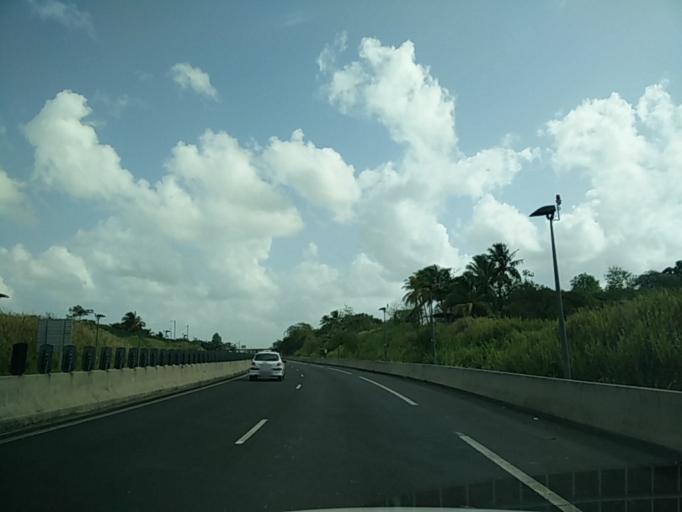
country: GP
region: Guadeloupe
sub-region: Guadeloupe
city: Les Abymes
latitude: 16.2602
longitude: -61.5108
